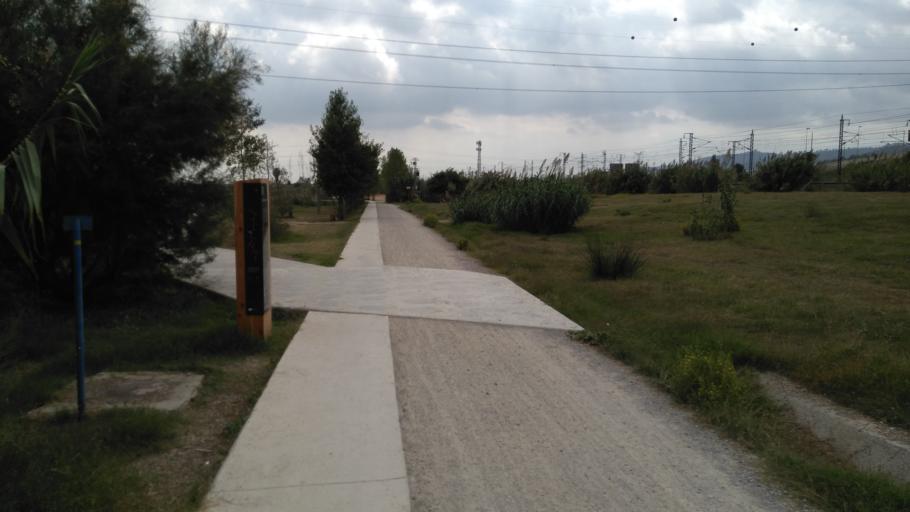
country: ES
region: Catalonia
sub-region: Provincia de Barcelona
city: Sant Vicenc dels Horts
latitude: 41.3901
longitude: 2.0208
